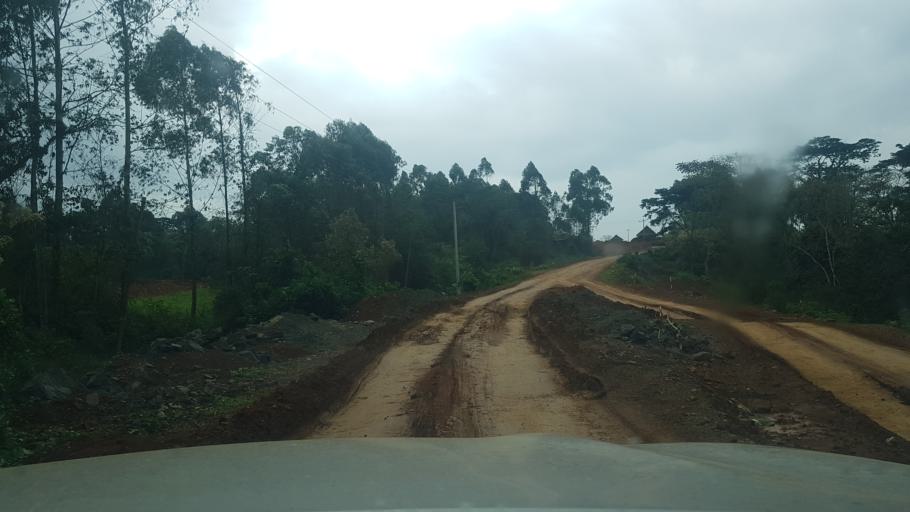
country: ET
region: Oromiya
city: Gore
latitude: 7.8912
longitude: 35.4870
